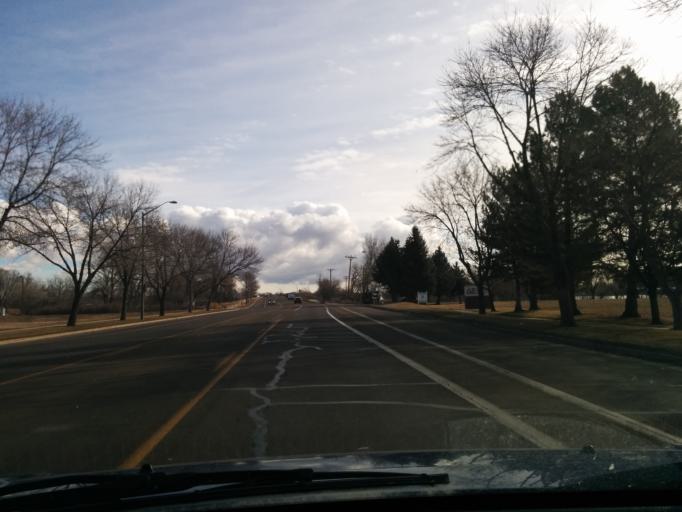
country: US
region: Colorado
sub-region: Larimer County
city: Fort Collins
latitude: 40.5671
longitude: -105.0311
